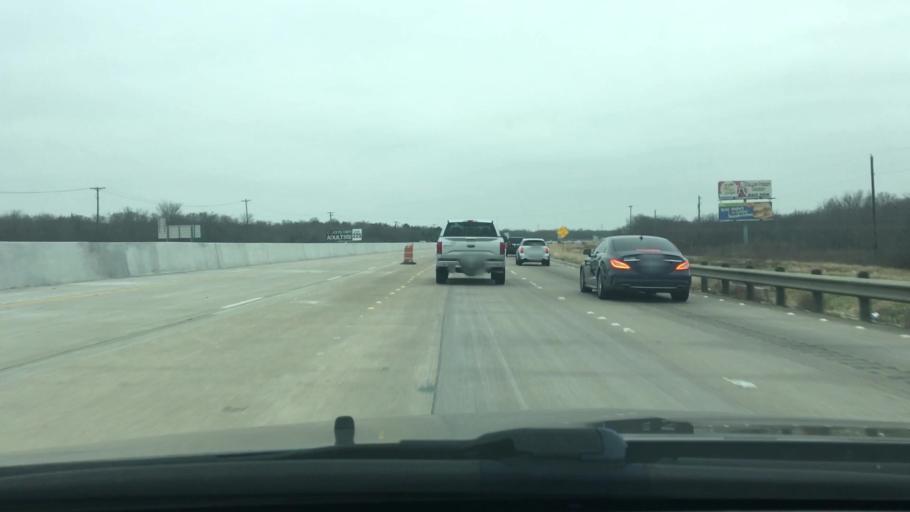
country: US
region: Texas
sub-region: Navarro County
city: Corsicana
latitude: 32.0895
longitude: -96.4394
